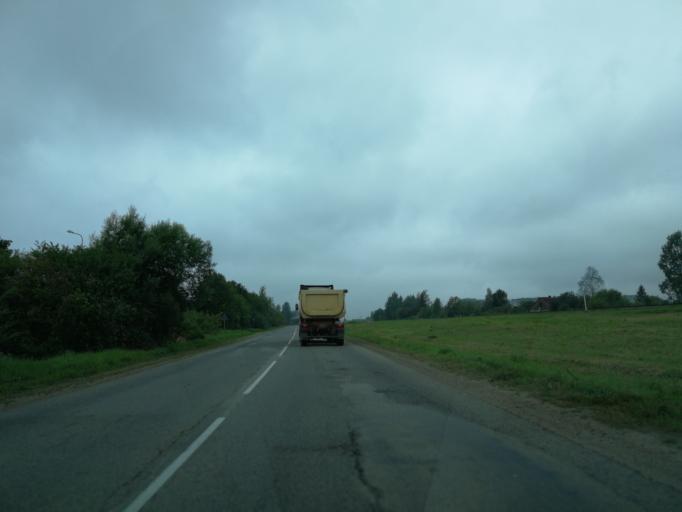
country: LV
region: Jekabpils Rajons
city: Jekabpils
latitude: 56.5020
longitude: 25.8973
